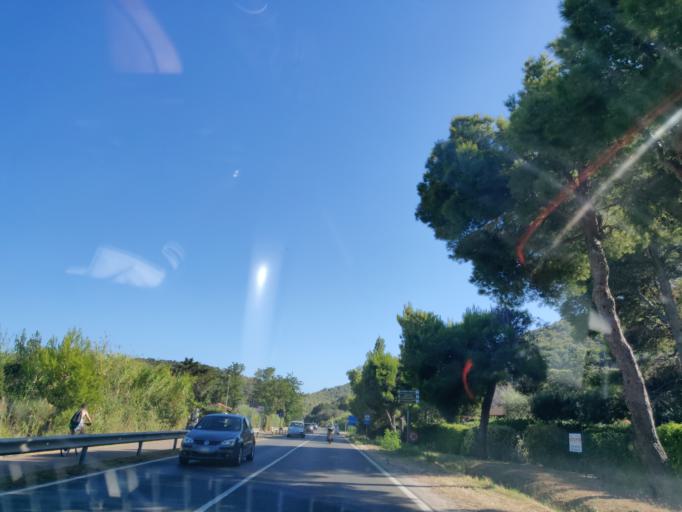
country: IT
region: Tuscany
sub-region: Provincia di Grosseto
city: Porto Ercole
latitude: 42.4191
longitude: 11.2032
